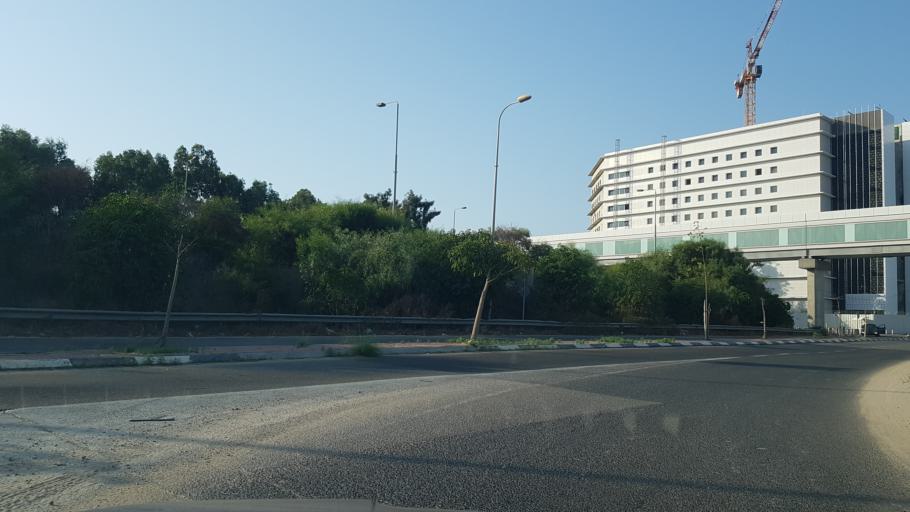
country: IL
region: Tel Aviv
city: Herzliyya
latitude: 32.1421
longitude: 34.8062
